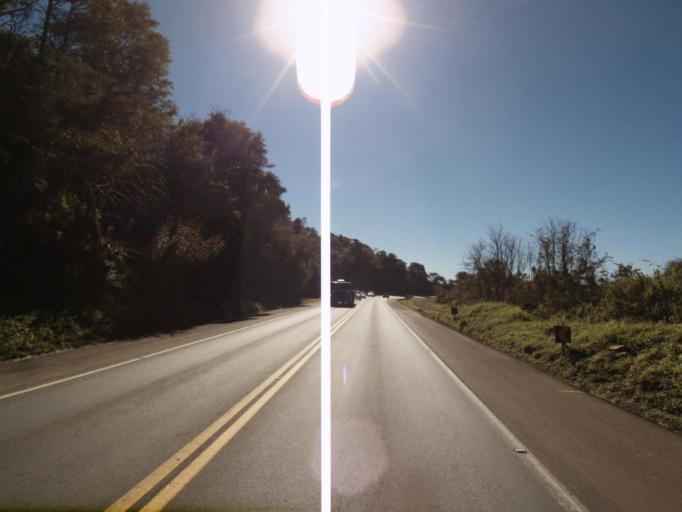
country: BR
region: Santa Catarina
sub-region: Chapeco
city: Chapeco
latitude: -26.9773
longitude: -52.5883
